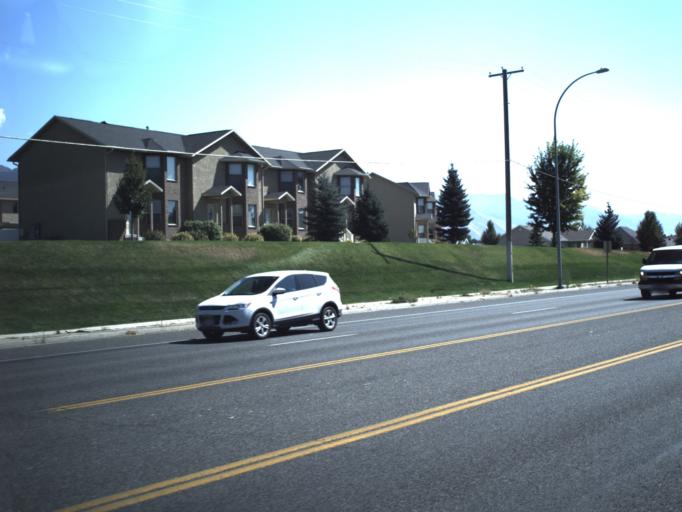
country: US
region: Utah
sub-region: Cache County
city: Smithfield
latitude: 41.8509
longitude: -111.8321
